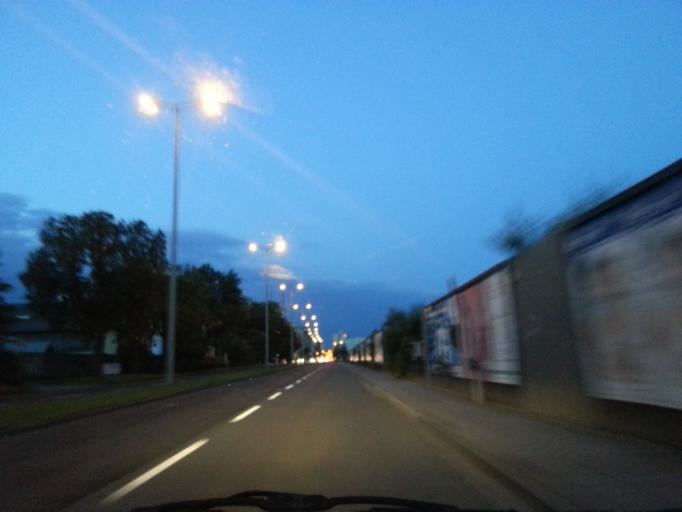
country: AT
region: Styria
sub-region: Graz Stadt
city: Goesting
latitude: 47.0787
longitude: 15.4161
